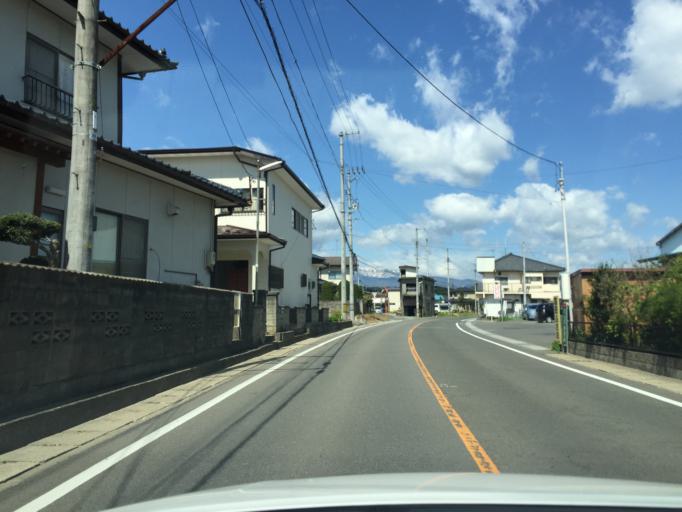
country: JP
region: Fukushima
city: Nihommatsu
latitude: 37.6560
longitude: 140.4725
